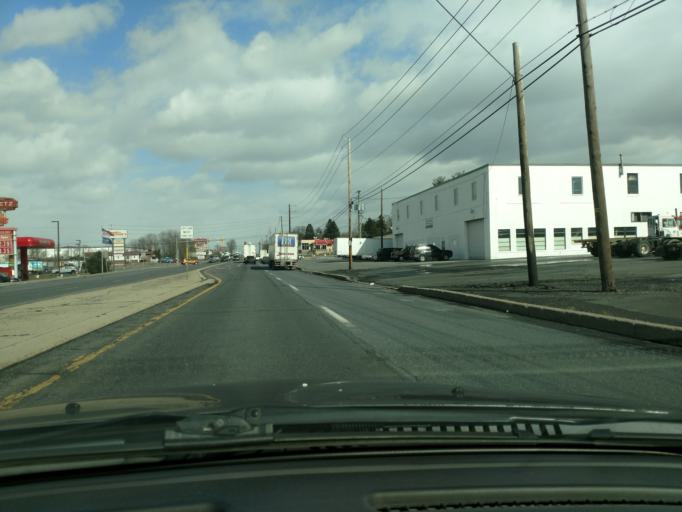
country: US
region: Pennsylvania
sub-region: Schuylkill County
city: Schuylkill Haven
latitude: 40.6404
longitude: -76.1601
